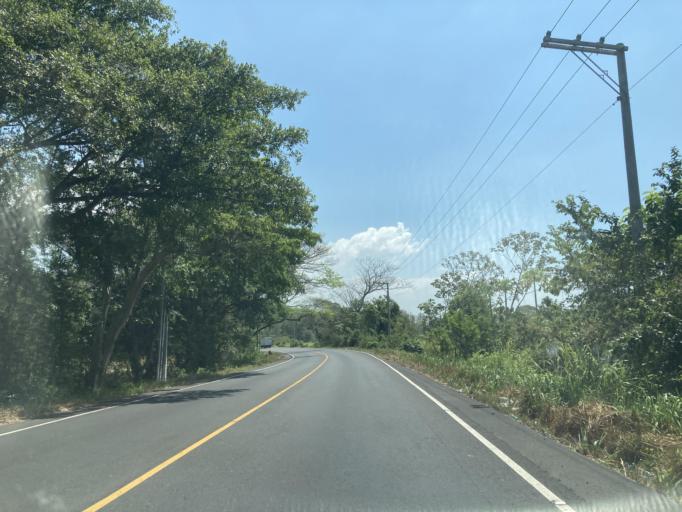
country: GT
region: Escuintla
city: Guanagazapa
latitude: 14.0970
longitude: -90.6020
